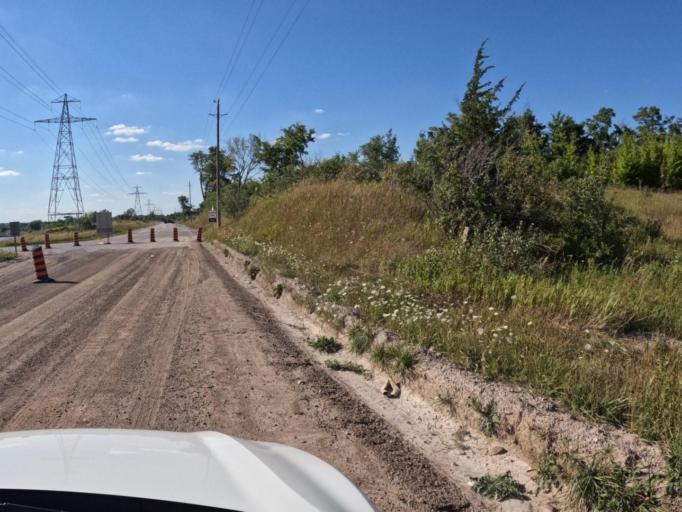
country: CA
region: Ontario
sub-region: Wellington County
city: Guelph
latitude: 43.4446
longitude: -80.1492
